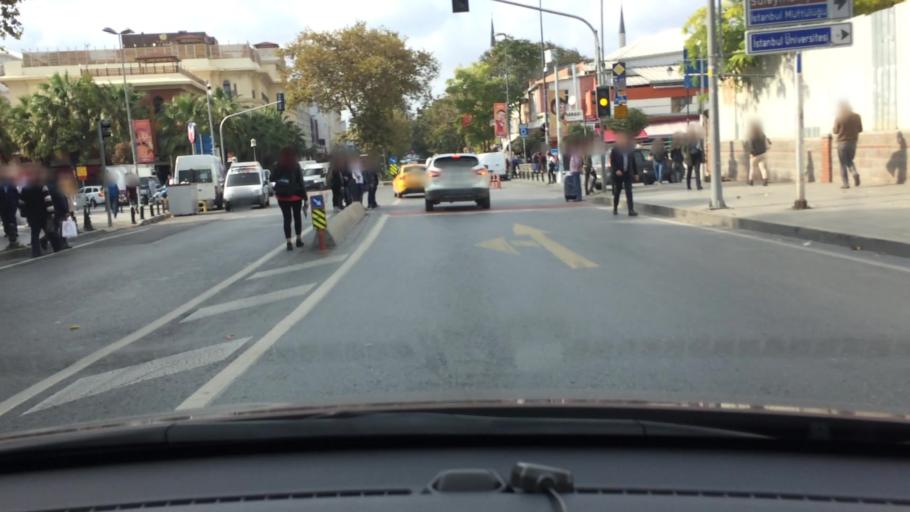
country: TR
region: Istanbul
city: Istanbul
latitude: 41.0120
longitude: 28.9599
